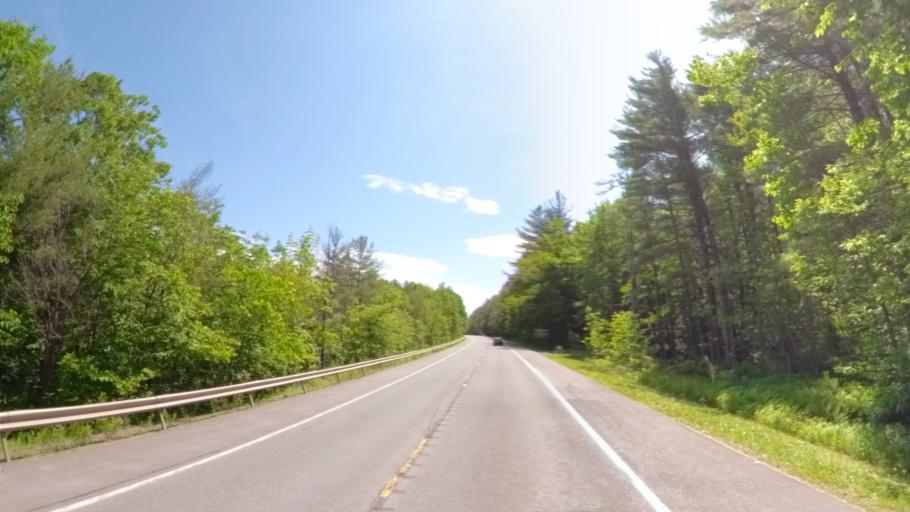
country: US
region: New York
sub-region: Ulster County
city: Shokan
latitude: 42.1151
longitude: -74.4190
